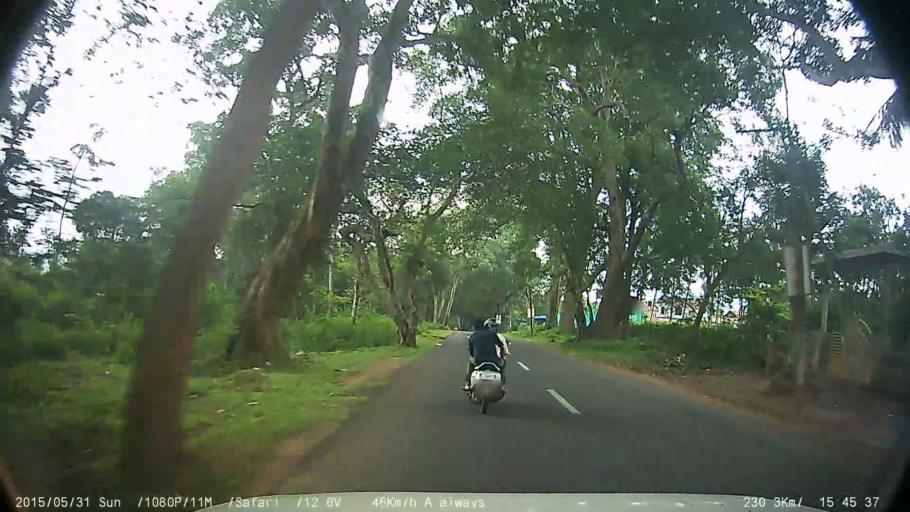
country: IN
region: Kerala
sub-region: Wayanad
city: Panamaram
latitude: 11.6744
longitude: 76.2971
